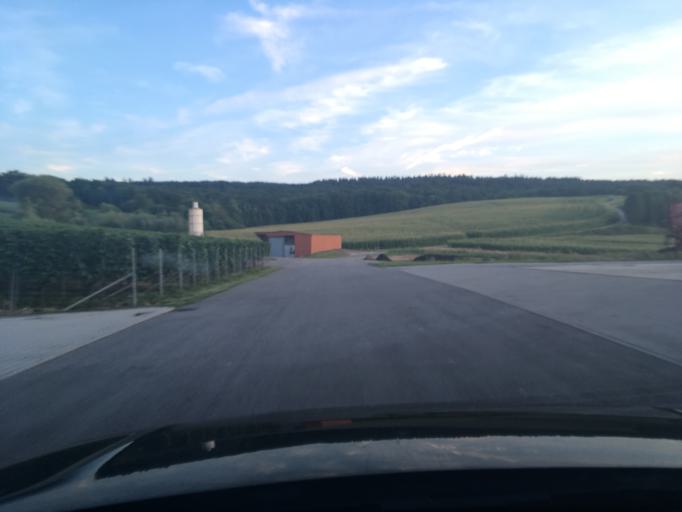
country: DE
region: Baden-Wuerttemberg
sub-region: Regierungsbezirk Stuttgart
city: Schwaigern
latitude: 49.1289
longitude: 9.0473
